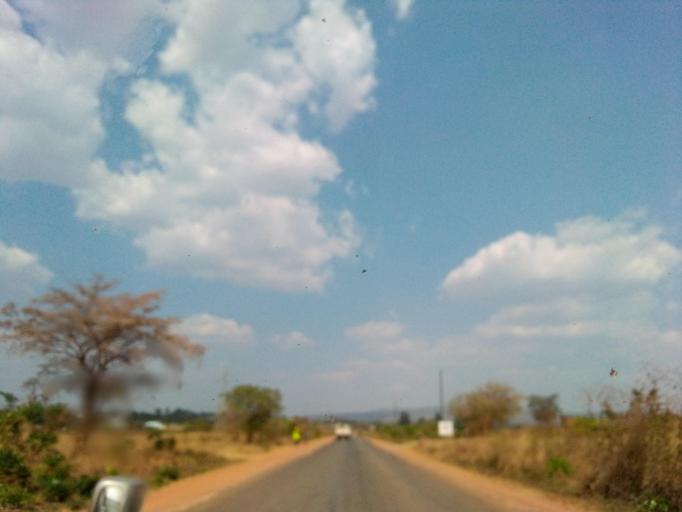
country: ZM
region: Northern
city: Mpika
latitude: -11.8330
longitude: 31.4143
